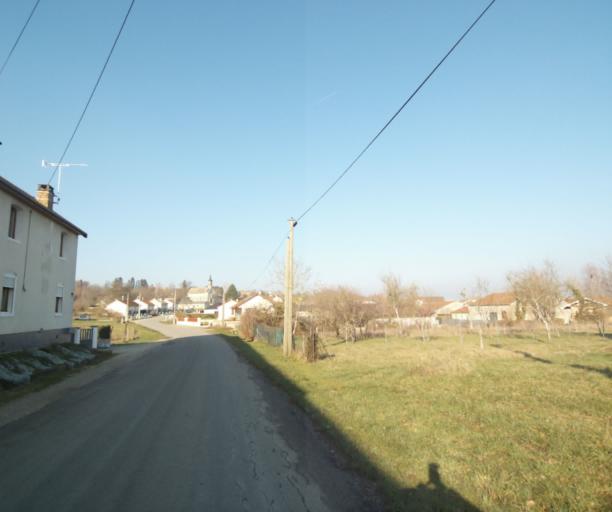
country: FR
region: Champagne-Ardenne
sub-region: Departement de la Haute-Marne
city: Wassy
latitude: 48.5114
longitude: 4.9190
